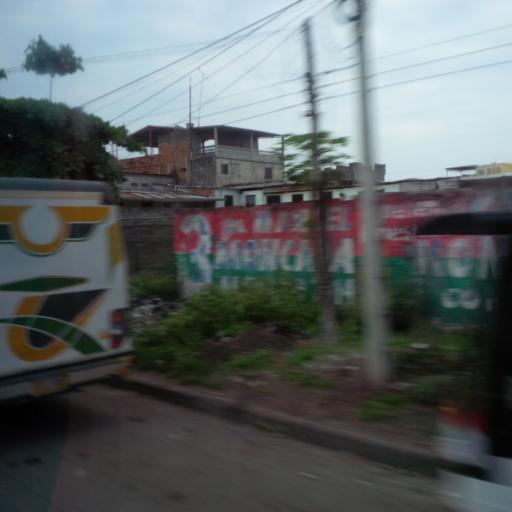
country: EC
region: Canar
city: La Troncal
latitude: -2.3319
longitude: -79.4035
